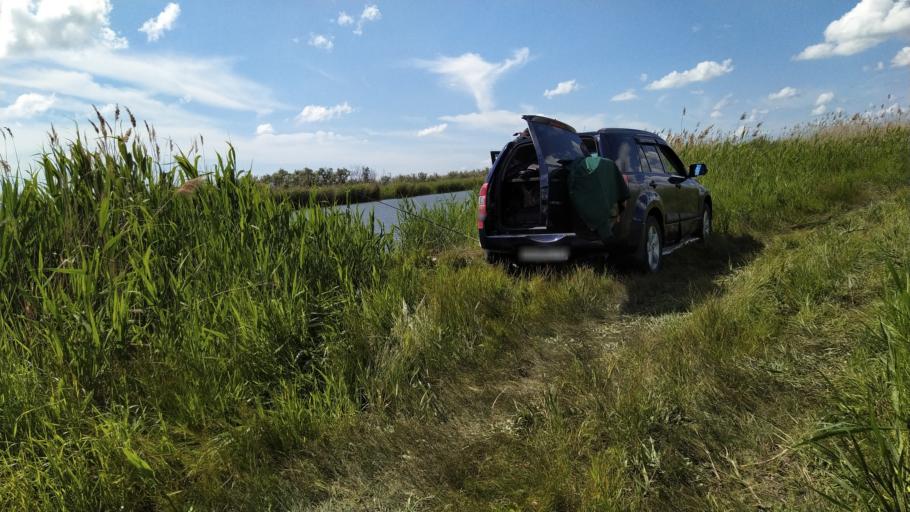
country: RU
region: Rostov
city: Bataysk
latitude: 47.1357
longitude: 39.6707
